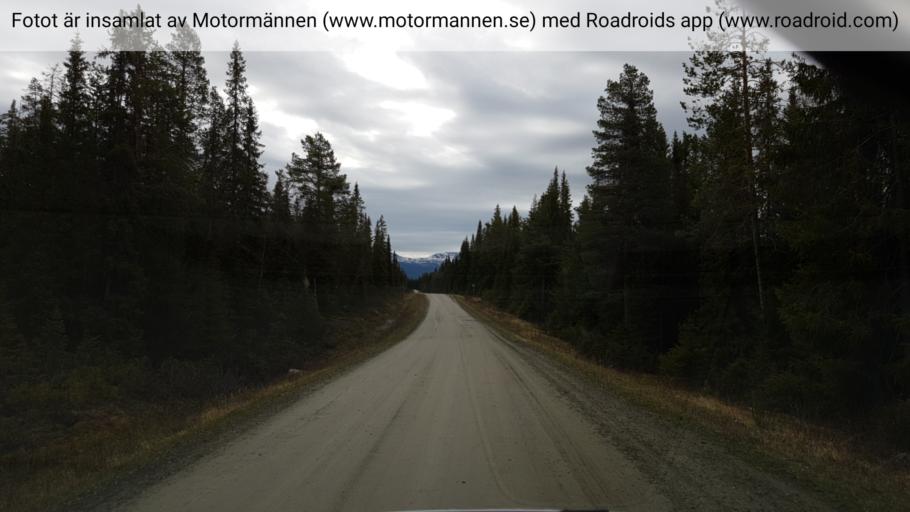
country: SE
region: Vaesterbotten
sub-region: Vilhelmina Kommun
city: Sjoberg
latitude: 65.5278
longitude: 15.4380
